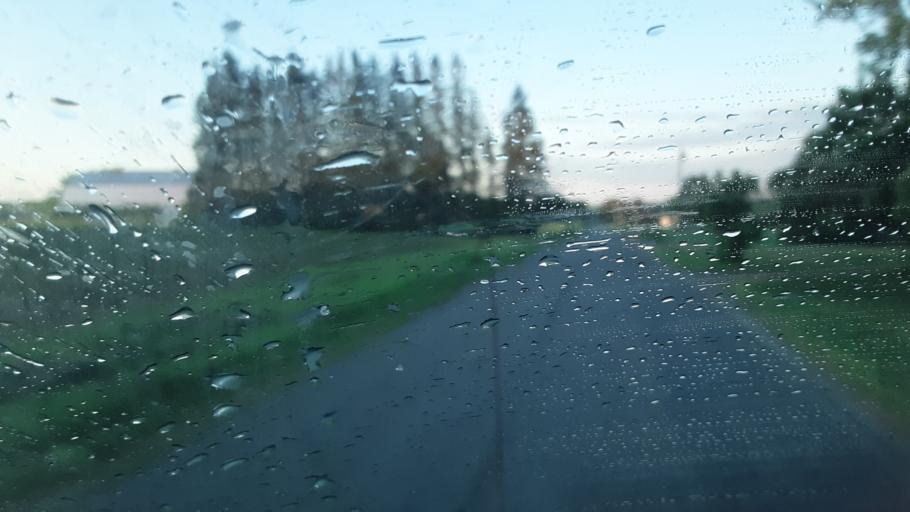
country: US
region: Maine
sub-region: Aroostook County
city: Caribou
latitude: 46.8341
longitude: -68.1359
